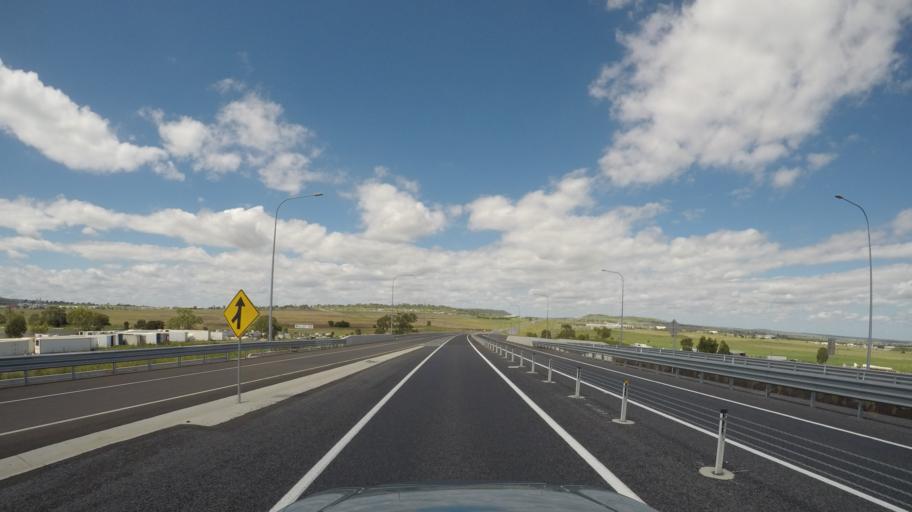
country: AU
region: Queensland
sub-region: Toowoomba
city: Wilsonton Heights
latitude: -27.5287
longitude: 151.8583
